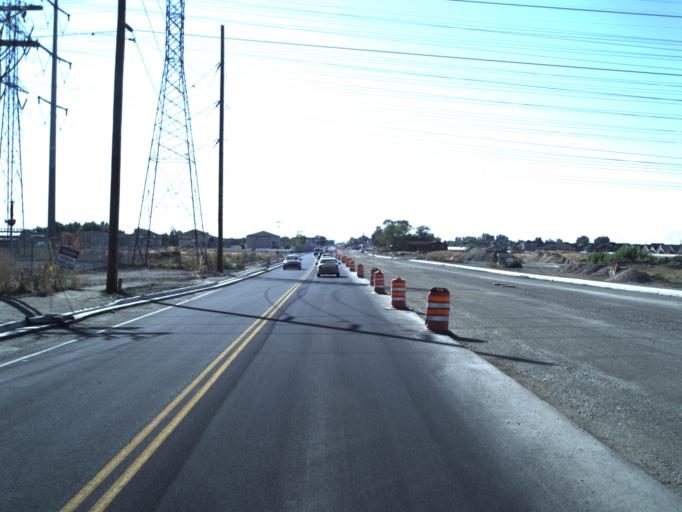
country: US
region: Utah
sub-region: Weber County
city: West Haven
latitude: 41.1907
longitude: -112.0565
